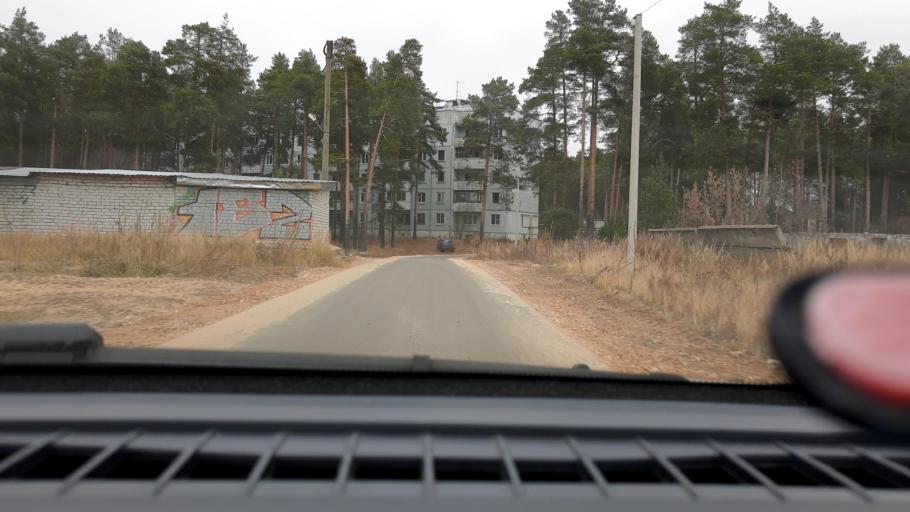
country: RU
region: Nizjnij Novgorod
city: Lukino
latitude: 56.3931
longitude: 43.7176
